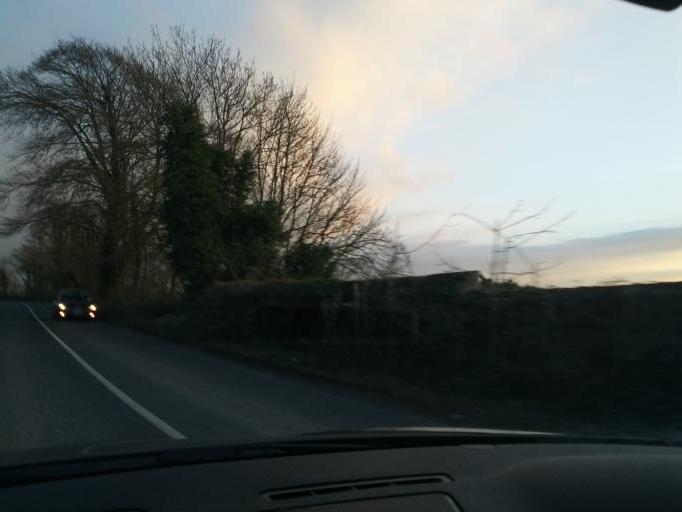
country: IE
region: Munster
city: Nenagh Bridge
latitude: 52.9165
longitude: -8.2164
